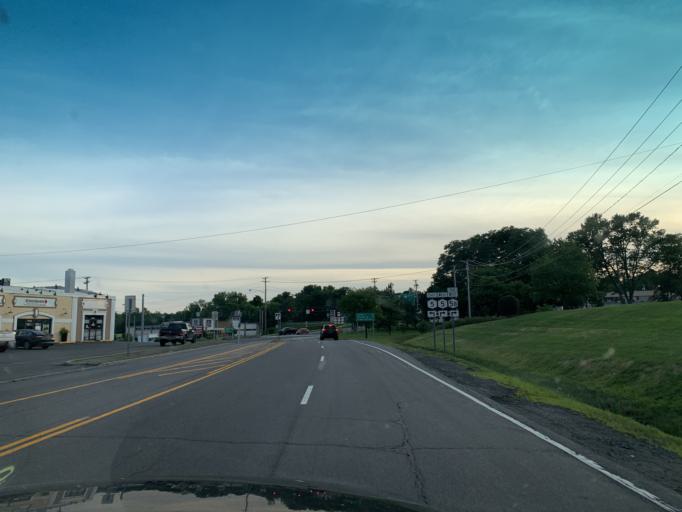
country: US
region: New York
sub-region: Oneida County
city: New Hartford
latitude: 43.0830
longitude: -75.3235
